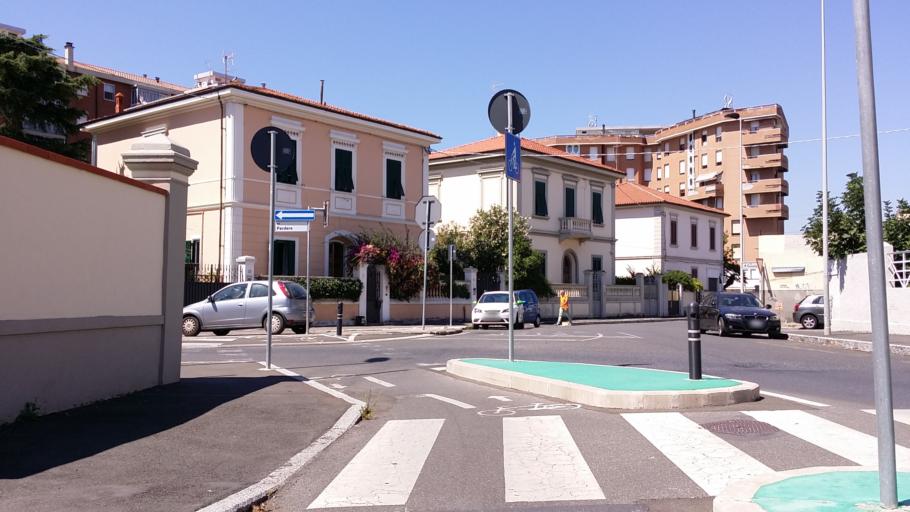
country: IT
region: Tuscany
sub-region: Provincia di Livorno
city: Livorno
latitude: 43.5414
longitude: 10.3263
